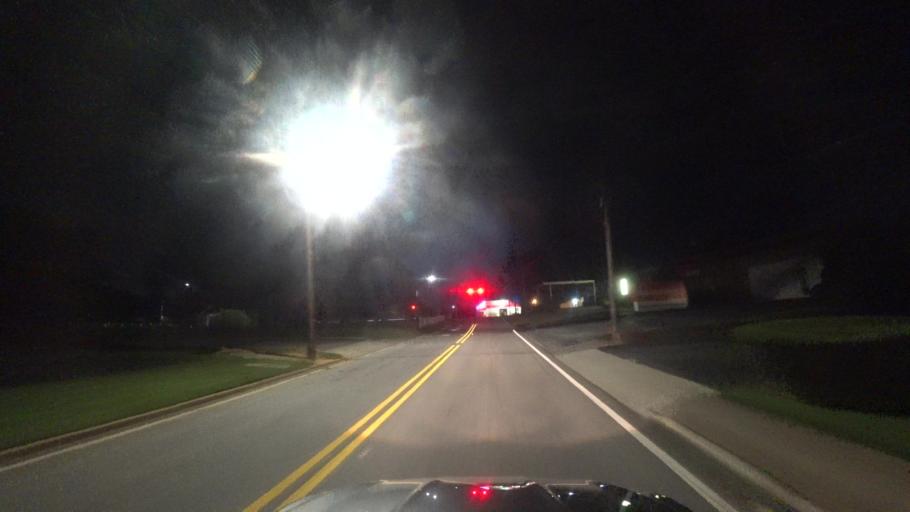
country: US
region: Georgia
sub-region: Clayton County
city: Forest Park
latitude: 33.6187
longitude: -84.3572
